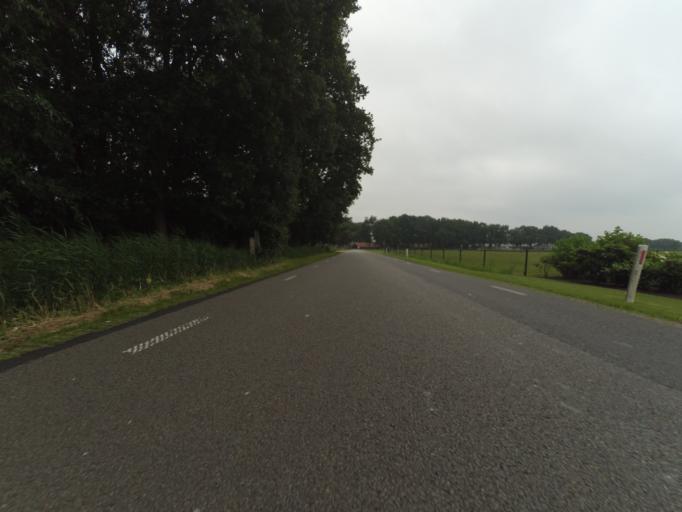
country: NL
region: Gelderland
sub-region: Gemeente Barneveld
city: Kootwijkerbroek
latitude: 52.1541
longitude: 5.6478
